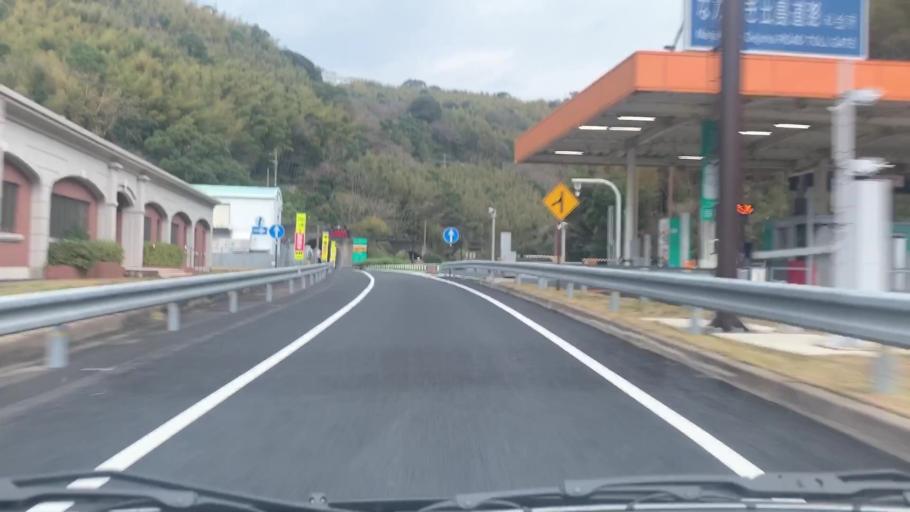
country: JP
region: Nagasaki
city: Nagasaki-shi
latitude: 32.7285
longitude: 129.9028
